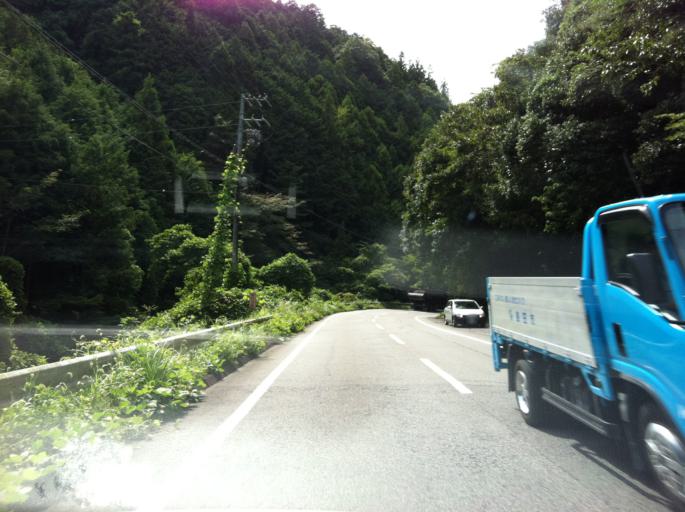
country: JP
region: Shizuoka
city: Kanaya
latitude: 34.9650
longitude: 138.0890
